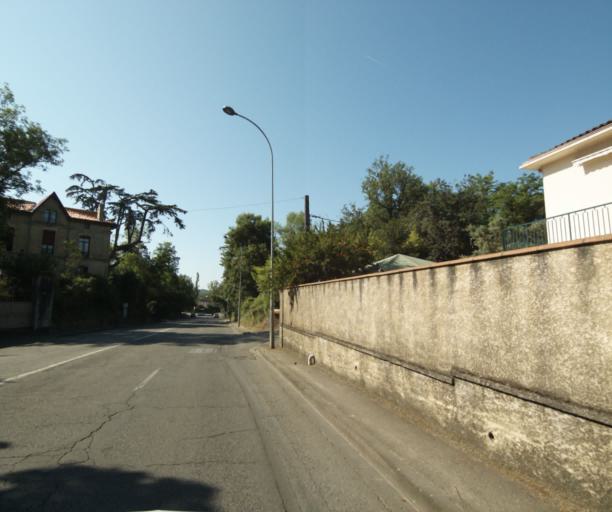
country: FR
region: Midi-Pyrenees
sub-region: Departement du Tarn-et-Garonne
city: Montauban
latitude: 44.0061
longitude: 1.3613
